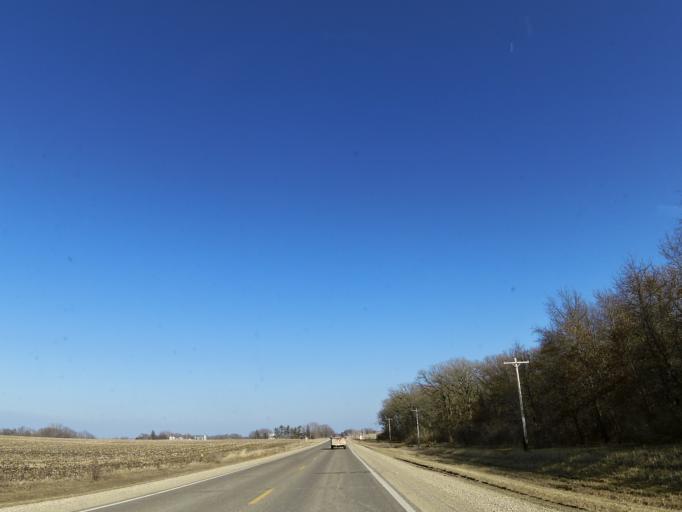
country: US
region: Iowa
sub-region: Worth County
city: Northwood
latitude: 43.4443
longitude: -93.3194
